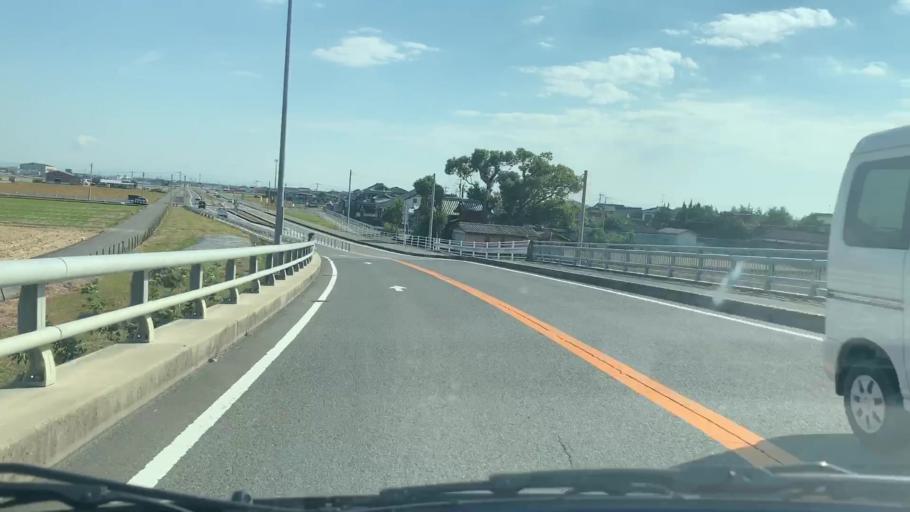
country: JP
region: Saga Prefecture
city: Saga-shi
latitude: 33.2215
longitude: 130.1953
